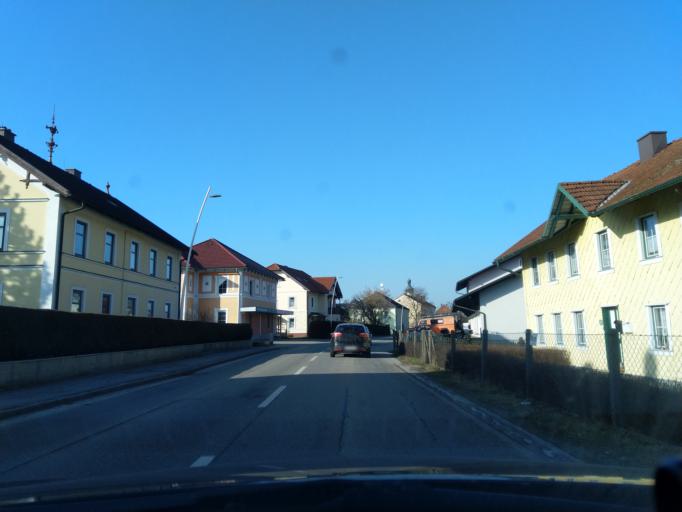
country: AT
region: Upper Austria
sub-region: Politischer Bezirk Ried im Innkreis
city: Ried im Innkreis
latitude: 48.2903
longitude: 13.4413
